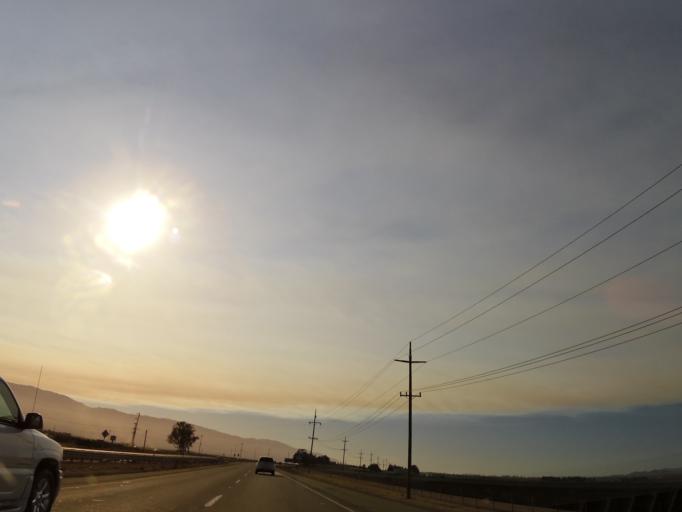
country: US
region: California
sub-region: Monterey County
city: Soledad
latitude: 36.4356
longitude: -121.3414
